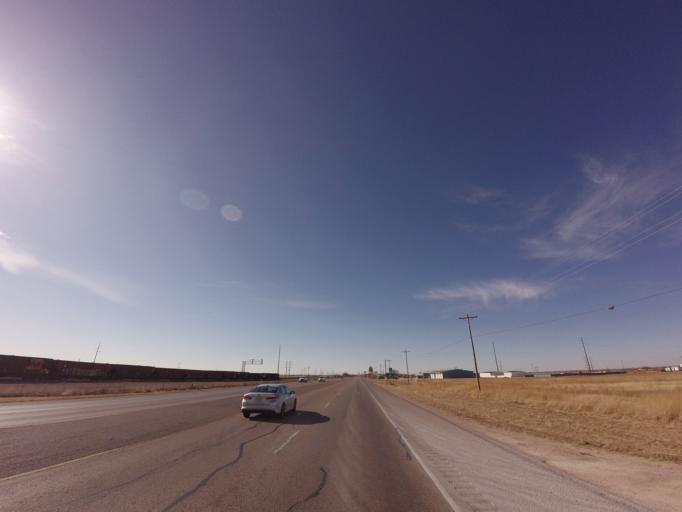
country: US
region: New Mexico
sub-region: Curry County
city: Clovis
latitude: 34.3938
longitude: -103.1386
